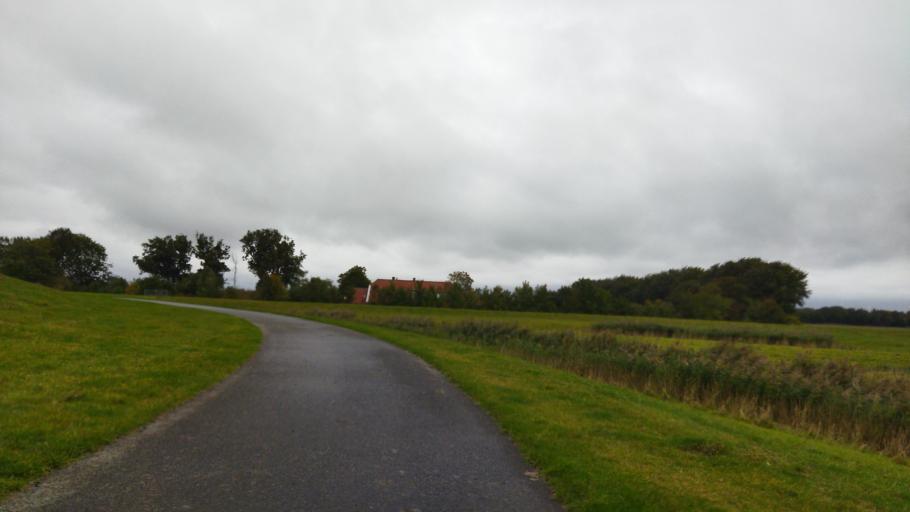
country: NL
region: Groningen
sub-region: Gemeente Delfzijl
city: Delfzijl
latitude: 53.4031
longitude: 7.0180
